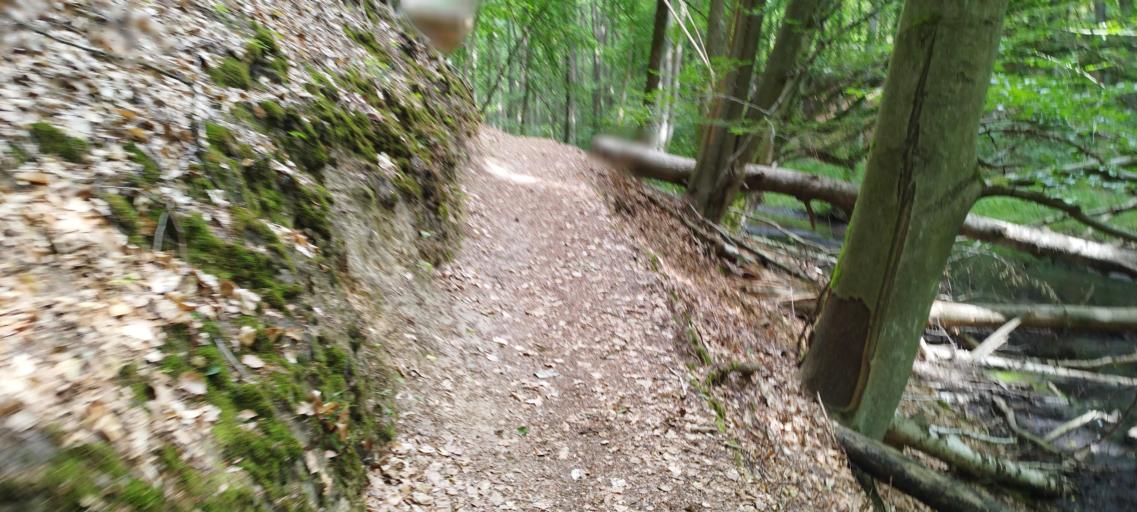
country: DE
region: Brandenburg
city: Mixdorf
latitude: 52.1285
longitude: 14.4654
